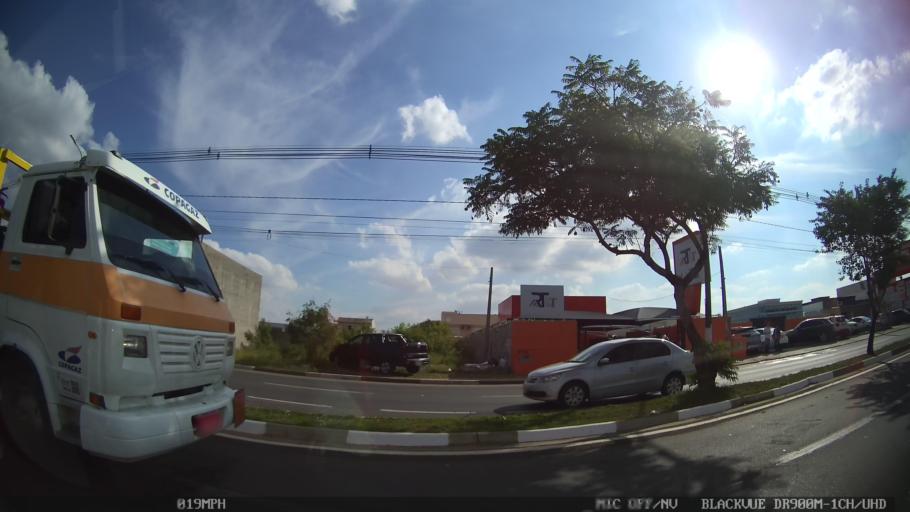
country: BR
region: Sao Paulo
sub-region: Hortolandia
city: Hortolandia
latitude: -22.8825
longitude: -47.2309
